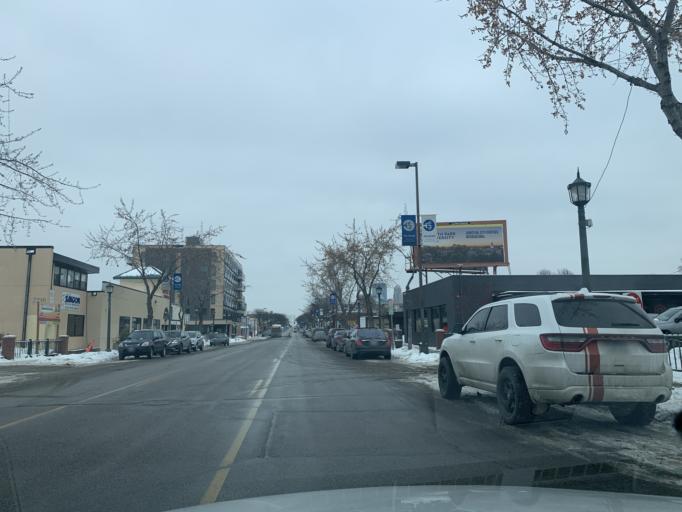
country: US
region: Minnesota
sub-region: Hennepin County
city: Minneapolis
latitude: 44.9527
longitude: -93.2779
